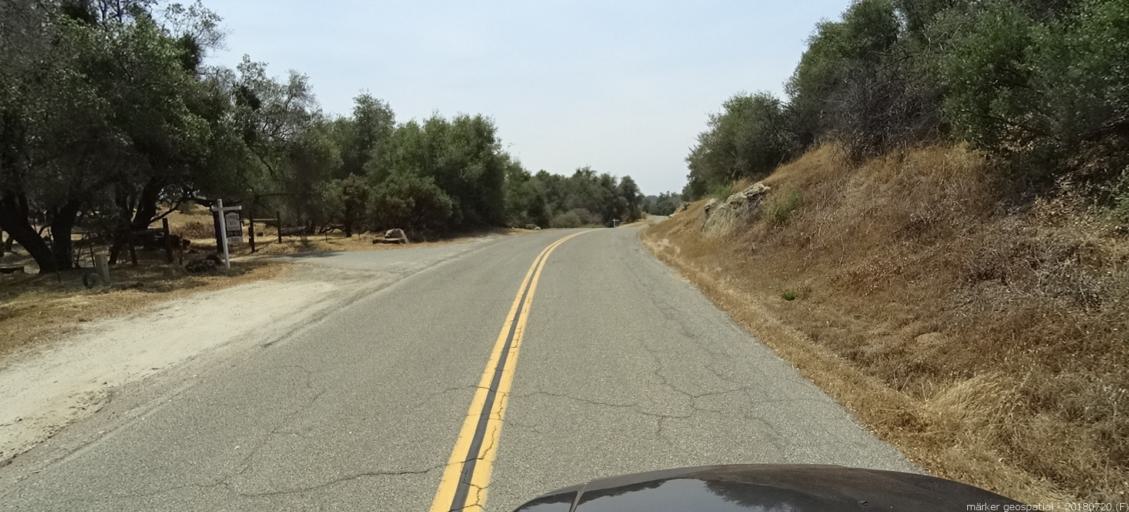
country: US
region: California
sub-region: Madera County
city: Ahwahnee
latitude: 37.3107
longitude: -119.7914
